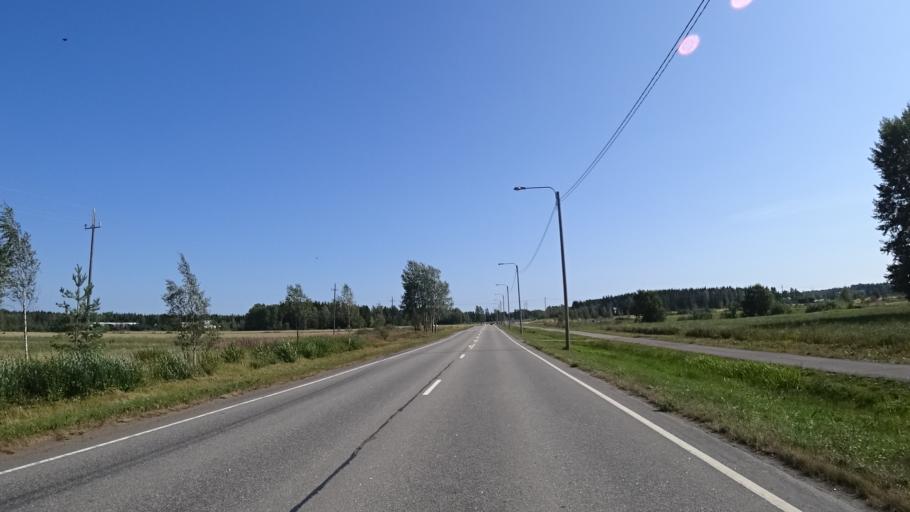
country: FI
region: Kymenlaakso
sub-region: Kotka-Hamina
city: Karhula
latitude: 60.5407
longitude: 26.9282
